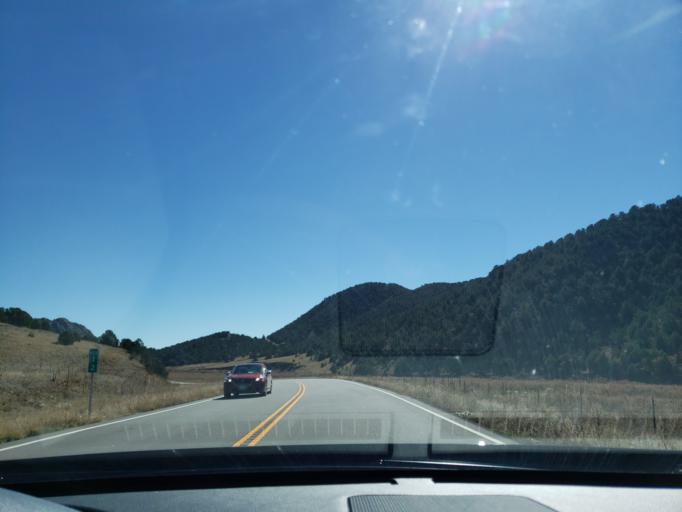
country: US
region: Colorado
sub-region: Fremont County
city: Canon City
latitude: 38.6235
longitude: -105.4562
